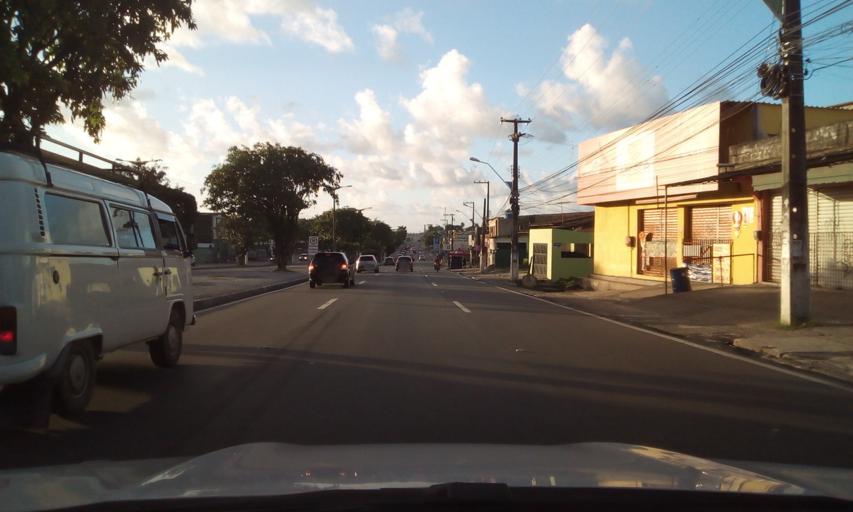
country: BR
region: Pernambuco
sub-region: Abreu E Lima
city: Abreu e Lima
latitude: -7.8993
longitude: -34.9023
